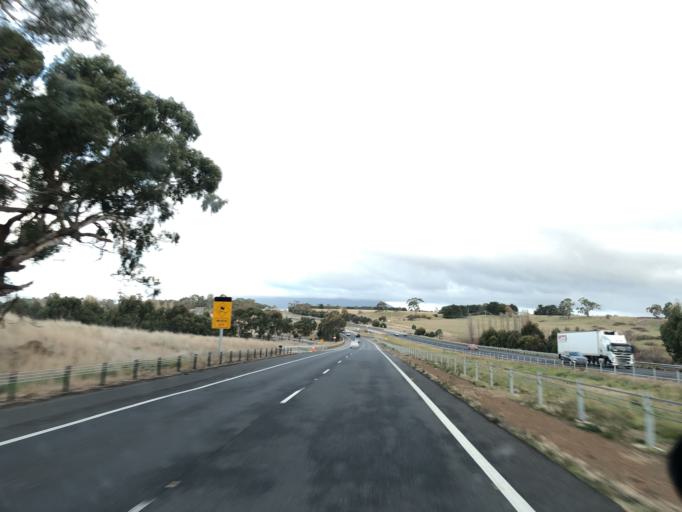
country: AU
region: Victoria
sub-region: Mount Alexander
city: Castlemaine
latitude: -37.2682
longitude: 144.4761
